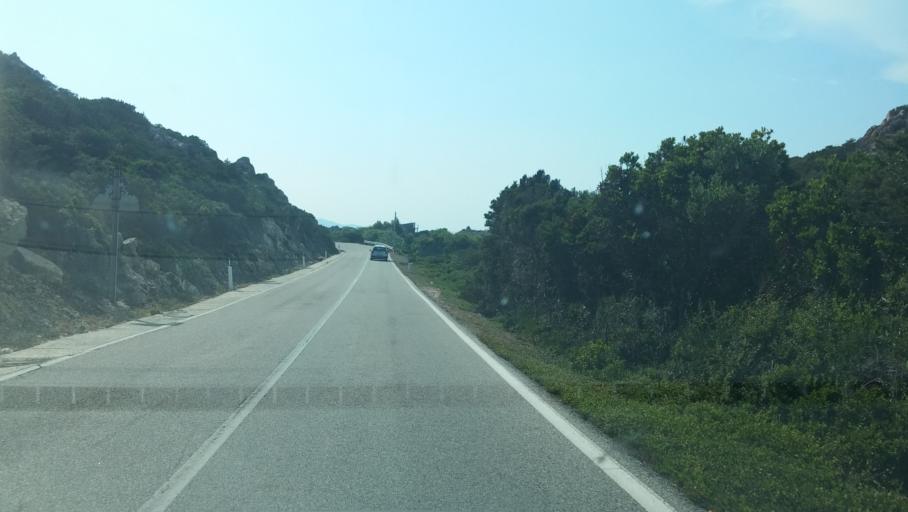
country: IT
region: Sardinia
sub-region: Provincia di Olbia-Tempio
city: La Maddalena
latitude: 41.2574
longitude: 9.4197
